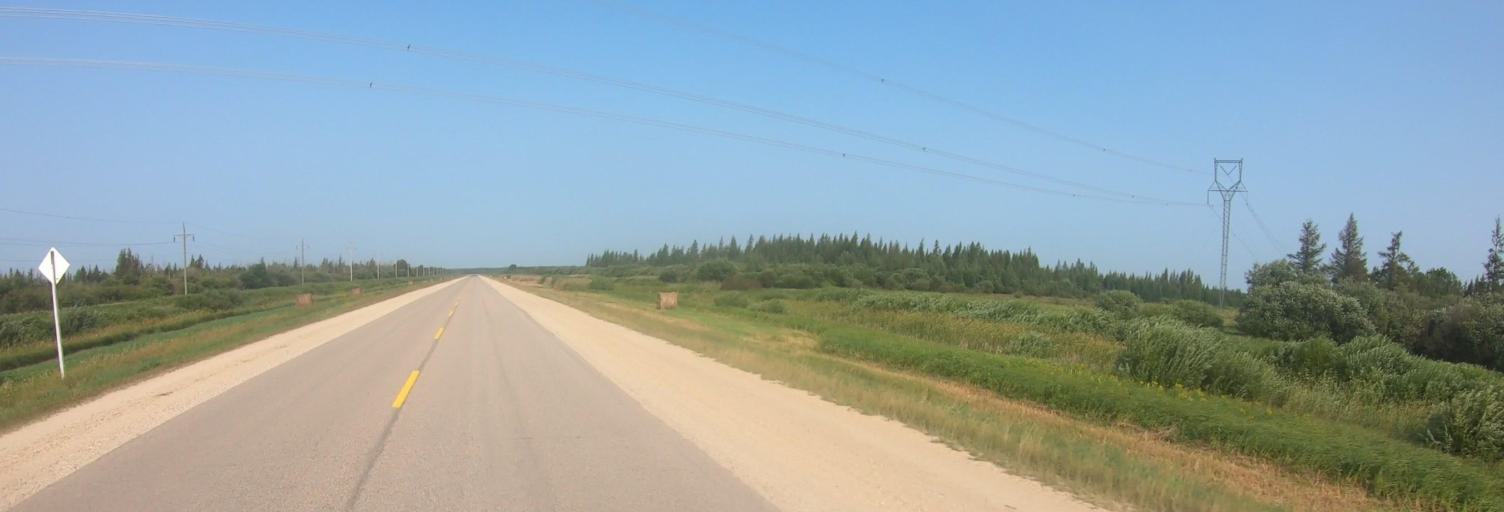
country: US
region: Minnesota
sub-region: Roseau County
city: Warroad
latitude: 49.0166
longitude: -95.5392
